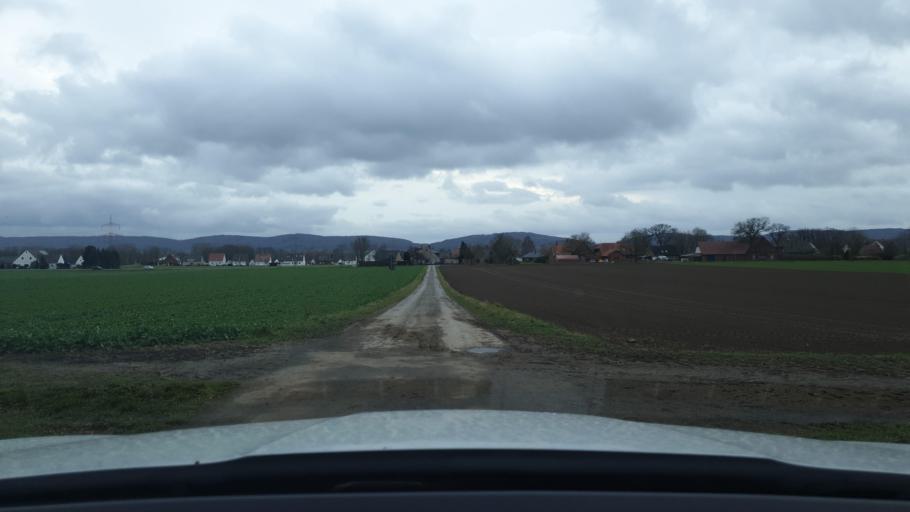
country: DE
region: North Rhine-Westphalia
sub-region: Regierungsbezirk Detmold
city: Hille
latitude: 52.3219
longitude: 8.8006
